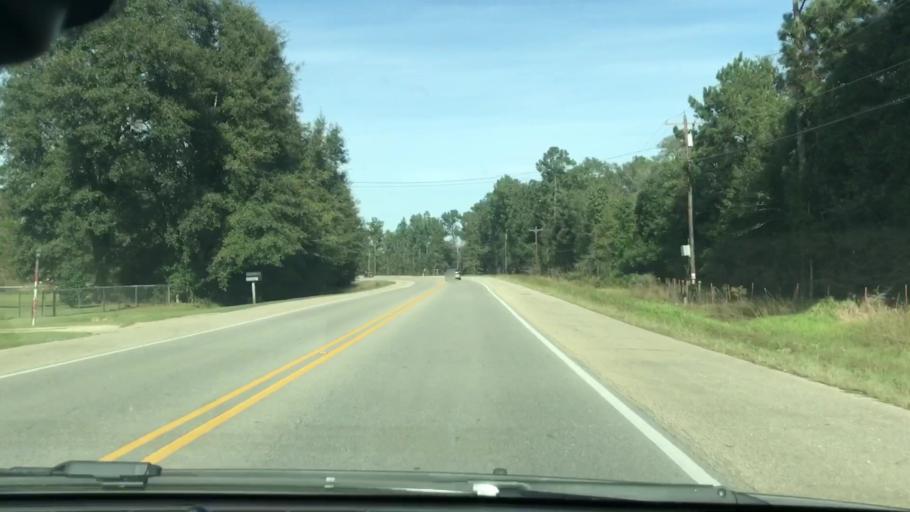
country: US
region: Louisiana
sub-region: Saint Tammany Parish
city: Pearl River
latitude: 30.4290
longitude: -89.7867
